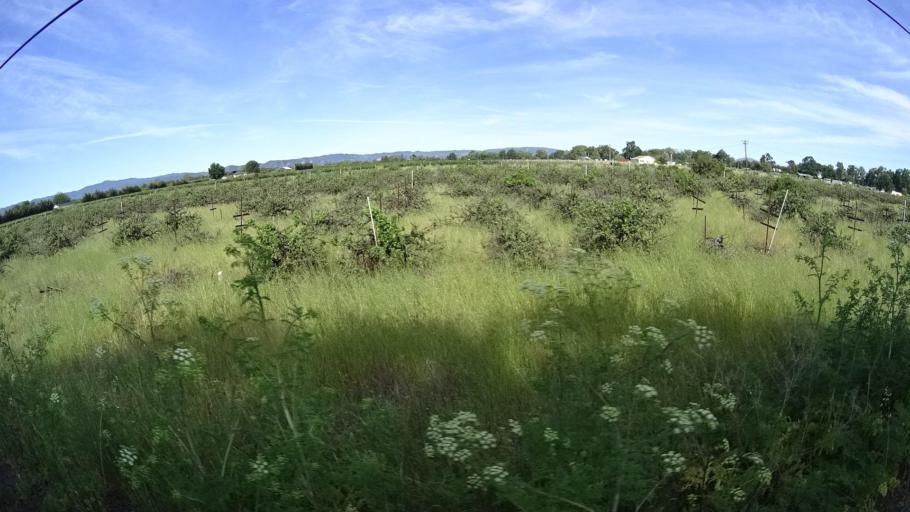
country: US
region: California
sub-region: Lake County
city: Kelseyville
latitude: 39.0087
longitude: -122.8243
